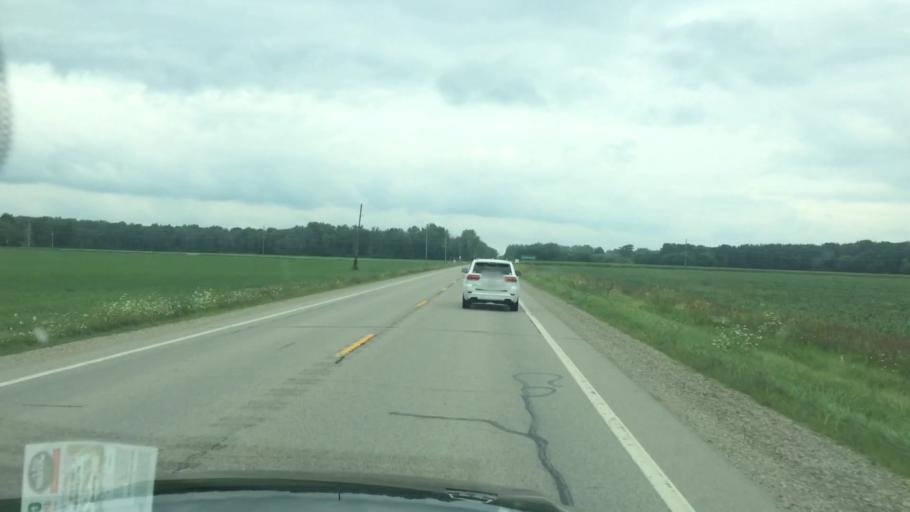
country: US
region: Michigan
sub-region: Tuscola County
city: Cass City
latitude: 43.4836
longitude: -83.0908
